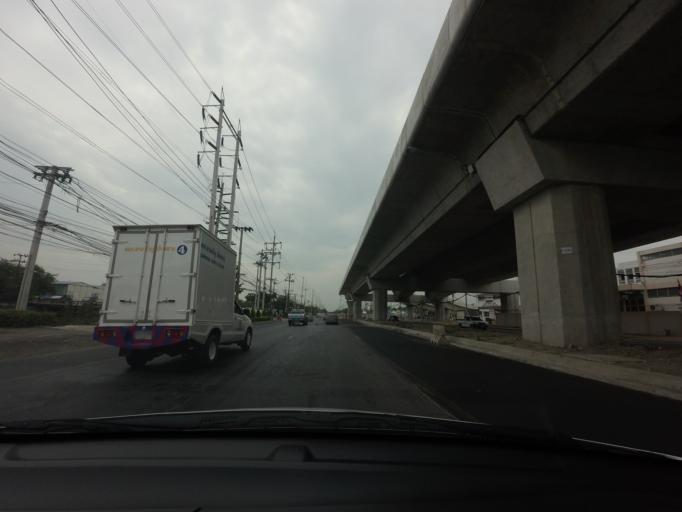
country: TH
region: Samut Prakan
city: Samut Prakan
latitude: 13.5588
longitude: 100.6121
